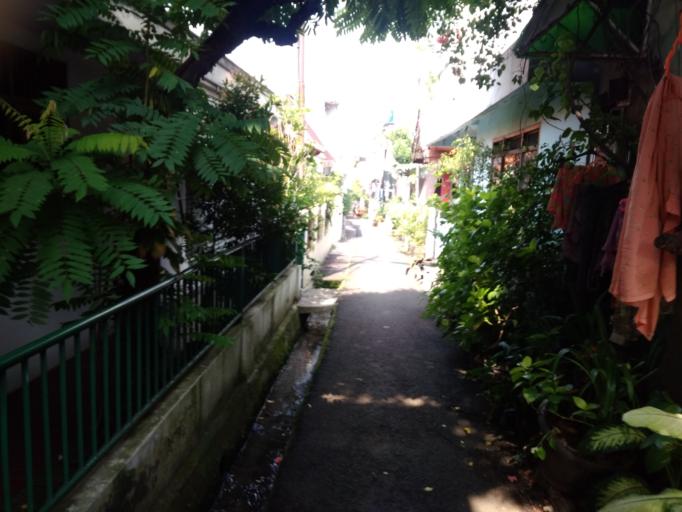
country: ID
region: Jakarta Raya
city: Jakarta
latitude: -6.2615
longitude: 106.7922
